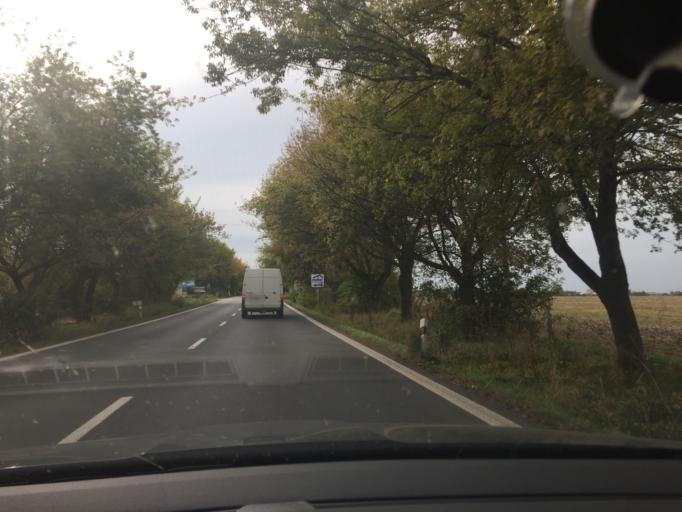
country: CZ
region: Central Bohemia
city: Zelenec
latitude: 50.1193
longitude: 14.6500
